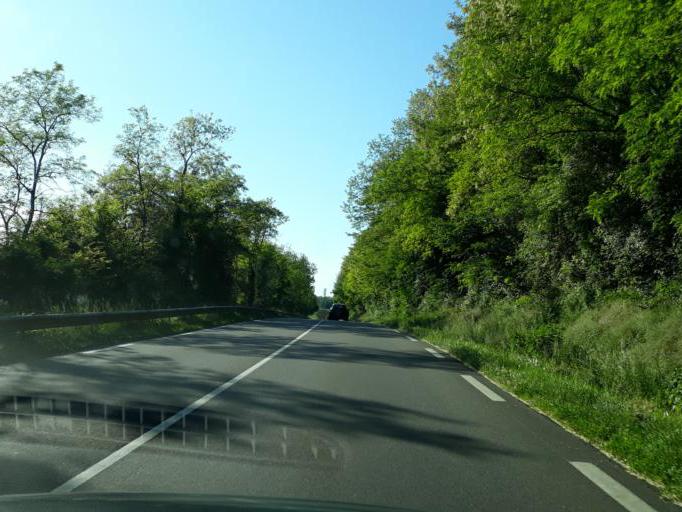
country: FR
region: Bourgogne
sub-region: Departement de la Nievre
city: Neuvy-sur-Loire
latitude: 47.5011
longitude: 2.9070
